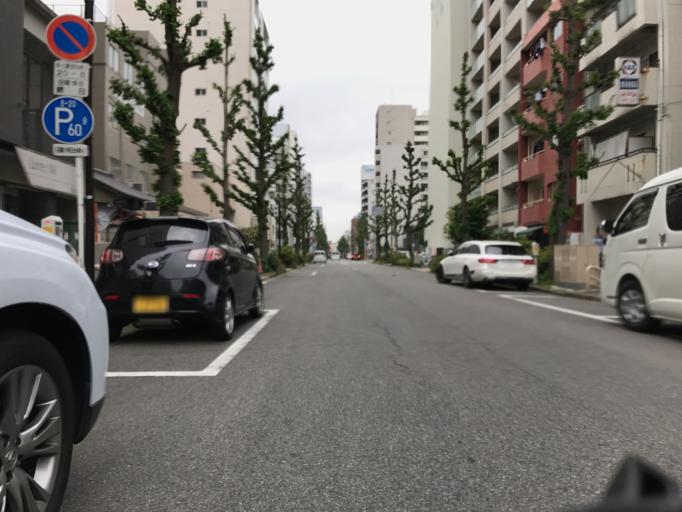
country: JP
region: Aichi
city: Nagoya-shi
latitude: 35.1755
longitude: 136.9050
